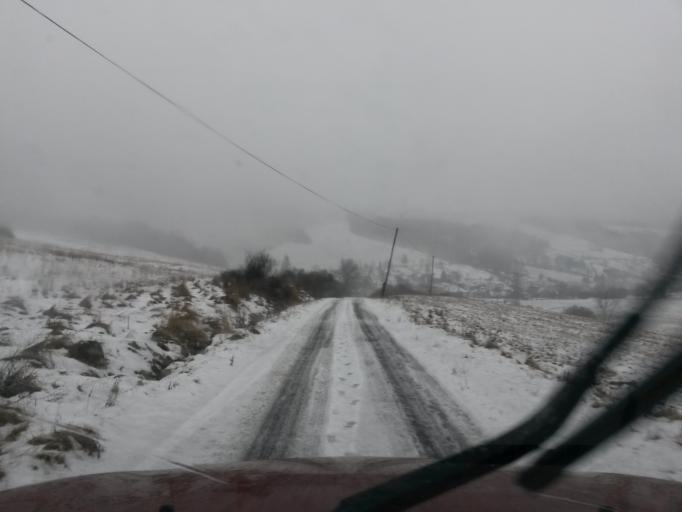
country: SK
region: Presovsky
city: Stropkov
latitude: 49.2460
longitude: 21.7480
